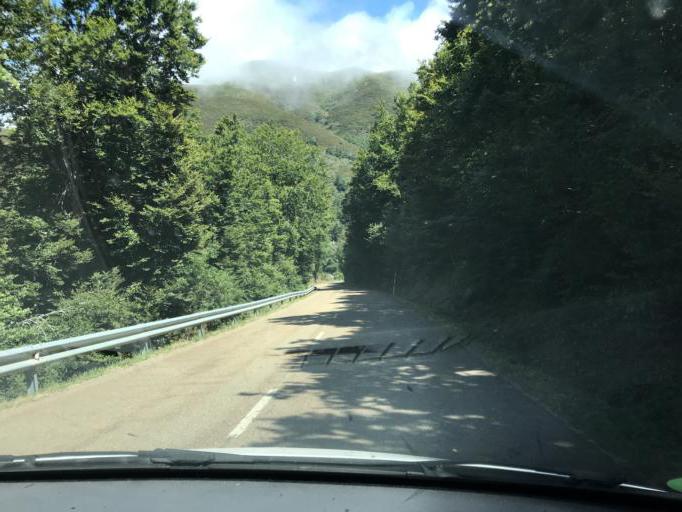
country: ES
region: Castille and Leon
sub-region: Provincia de Palencia
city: Polentinos
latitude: 43.0527
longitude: -4.4557
